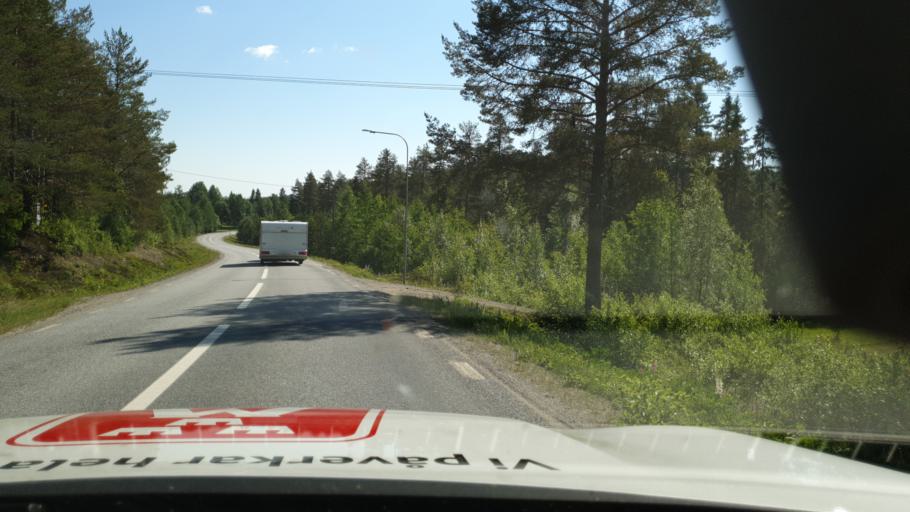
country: SE
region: Vaesterbotten
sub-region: Umea Kommun
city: Ersmark
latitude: 64.3311
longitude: 20.2258
